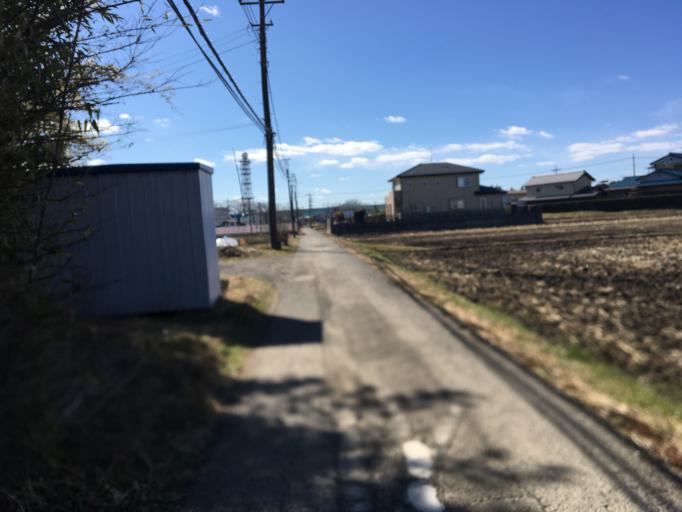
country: JP
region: Saitama
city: Shiki
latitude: 35.8493
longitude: 139.5765
